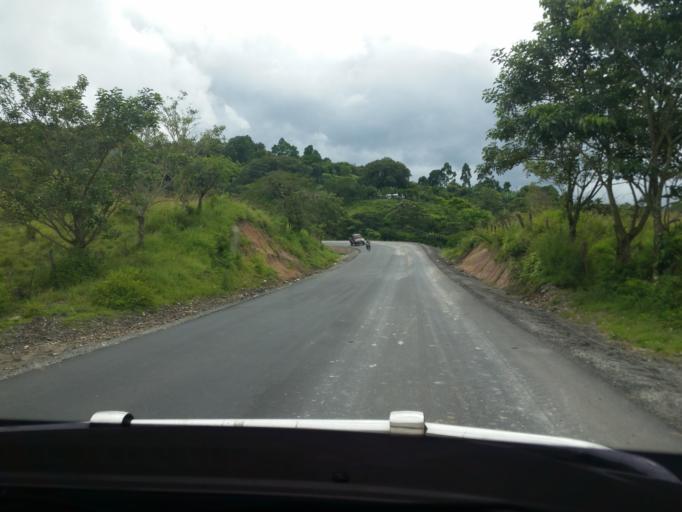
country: NI
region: Jinotega
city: Jinotega
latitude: 13.1671
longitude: -85.9243
